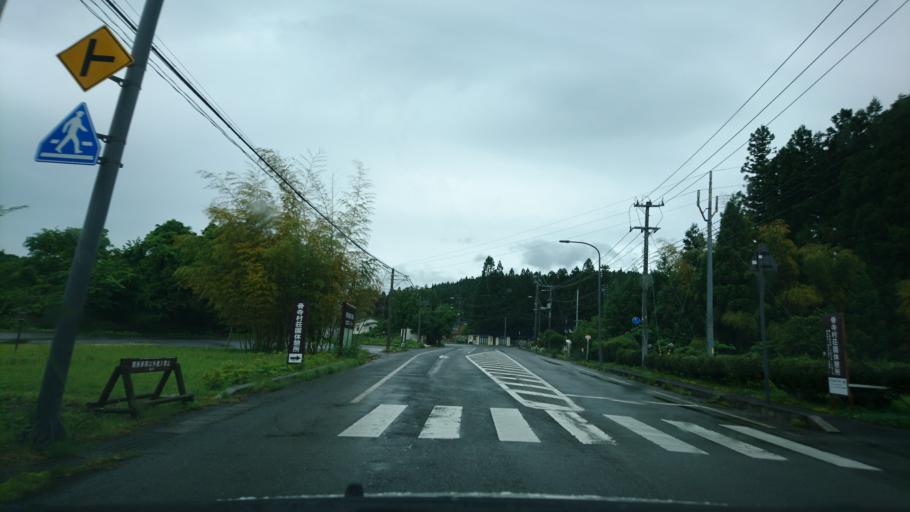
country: JP
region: Iwate
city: Ichinoseki
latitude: 38.9738
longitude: 140.9502
